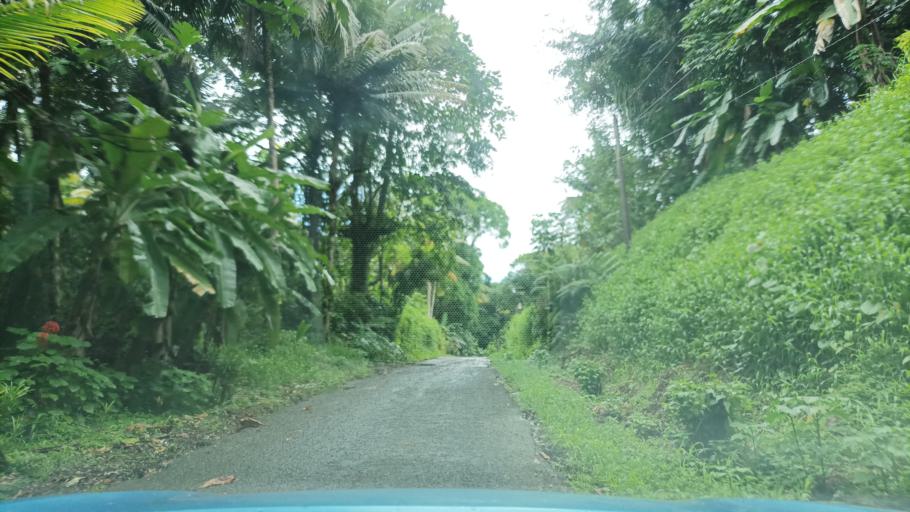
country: FM
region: Pohnpei
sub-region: Sokehs Municipality
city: Palikir - National Government Center
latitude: 6.8283
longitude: 158.1704
